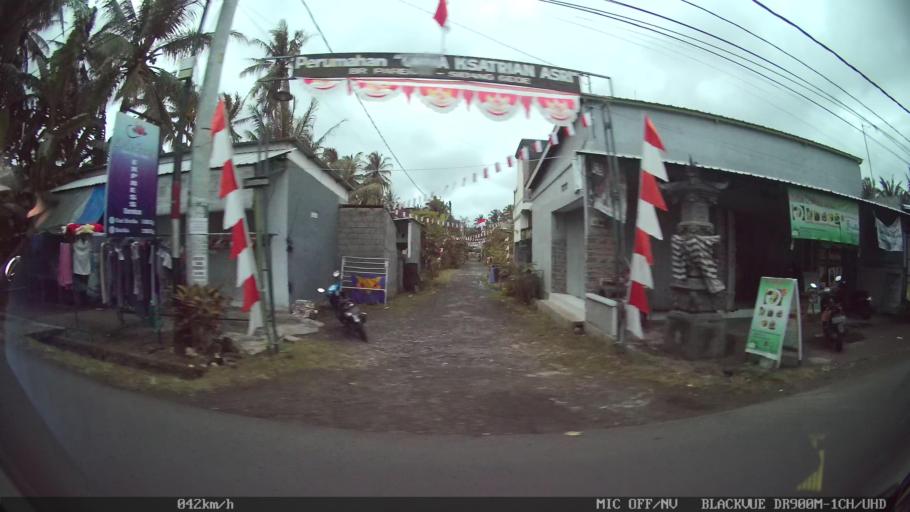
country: ID
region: Bali
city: Banjar Parekan
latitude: -8.5743
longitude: 115.2113
